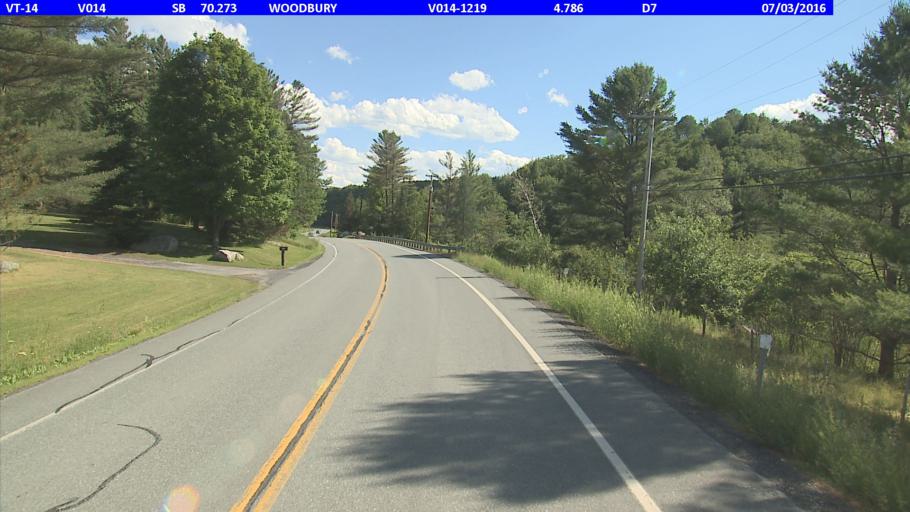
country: US
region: Vermont
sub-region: Caledonia County
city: Hardwick
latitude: 44.4564
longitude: -72.4200
